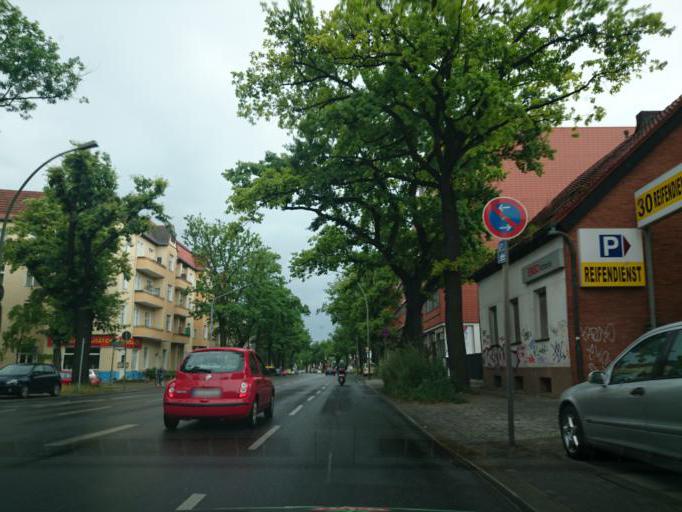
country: DE
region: Berlin
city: Mariendorf
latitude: 52.4367
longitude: 13.3795
